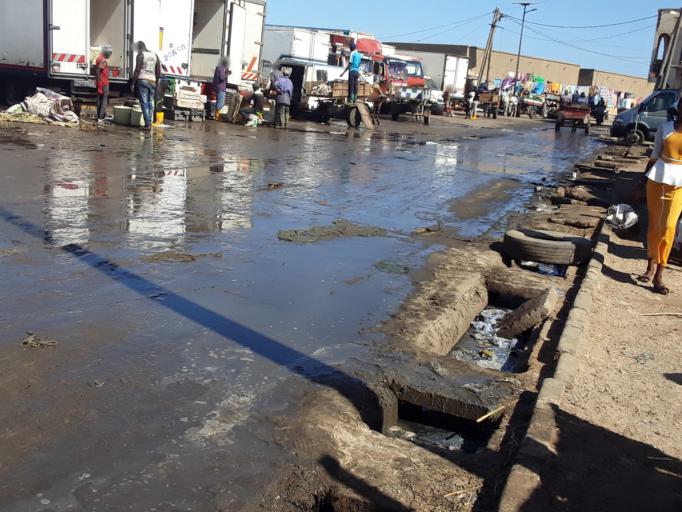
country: SN
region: Saint-Louis
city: Saint-Louis
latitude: 16.0180
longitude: -16.5090
